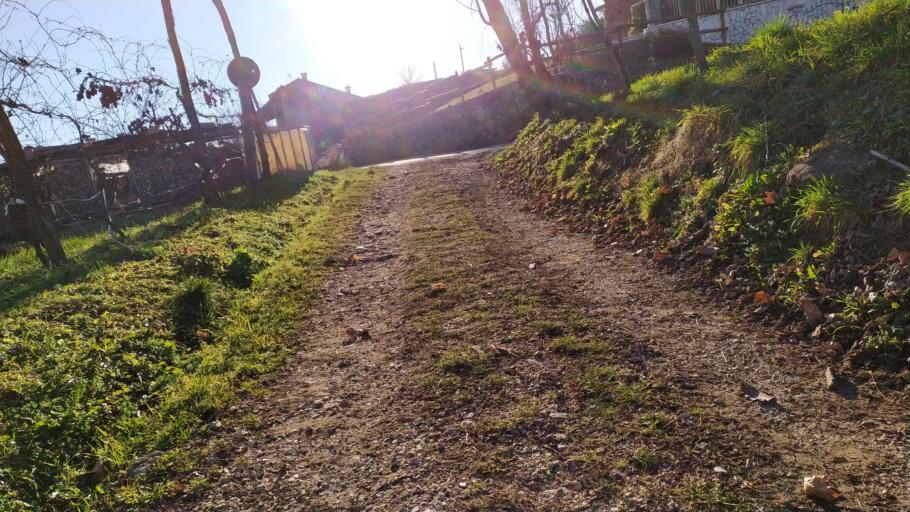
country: IT
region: Veneto
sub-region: Provincia di Vicenza
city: Monte di Malo
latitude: 45.6698
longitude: 11.3552
